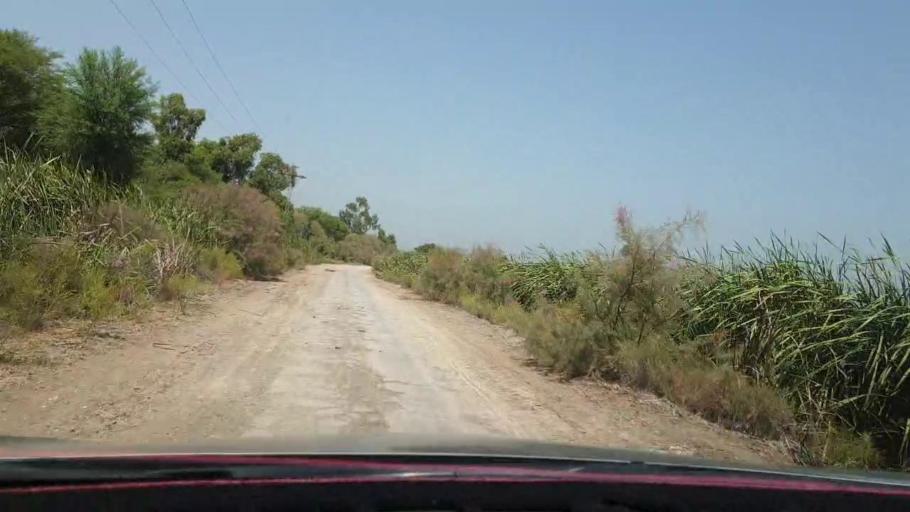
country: PK
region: Sindh
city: Warah
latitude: 27.4276
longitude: 67.6987
